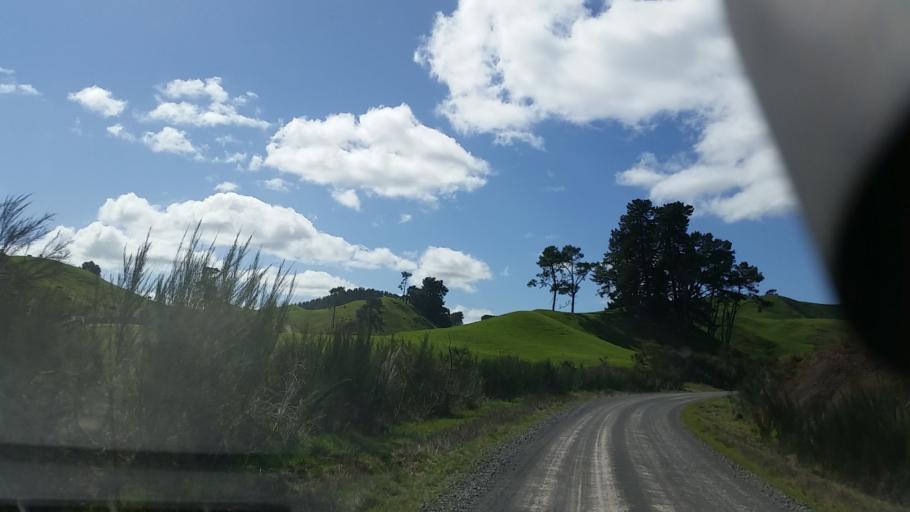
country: NZ
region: Waikato
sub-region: Taupo District
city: Taupo
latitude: -38.4980
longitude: 176.2029
